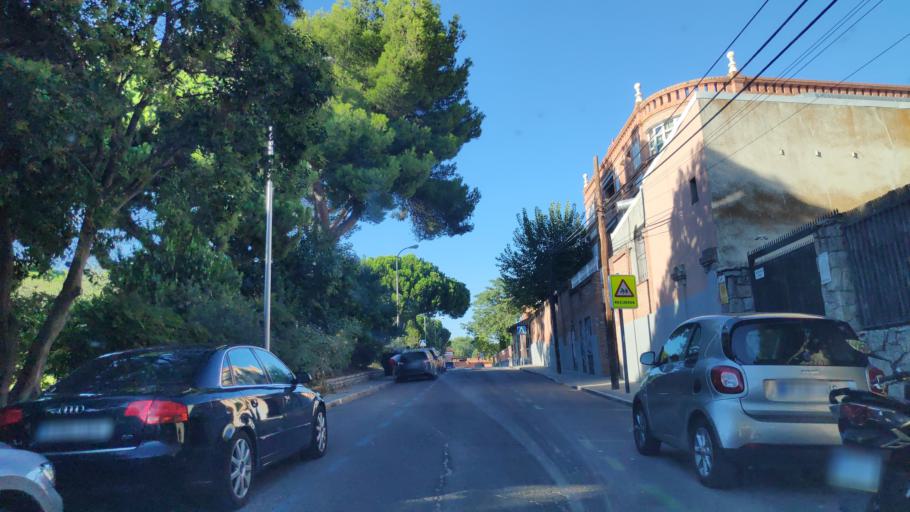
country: ES
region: Madrid
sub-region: Provincia de Madrid
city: Tetuan de las Victorias
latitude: 40.4574
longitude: -3.7164
